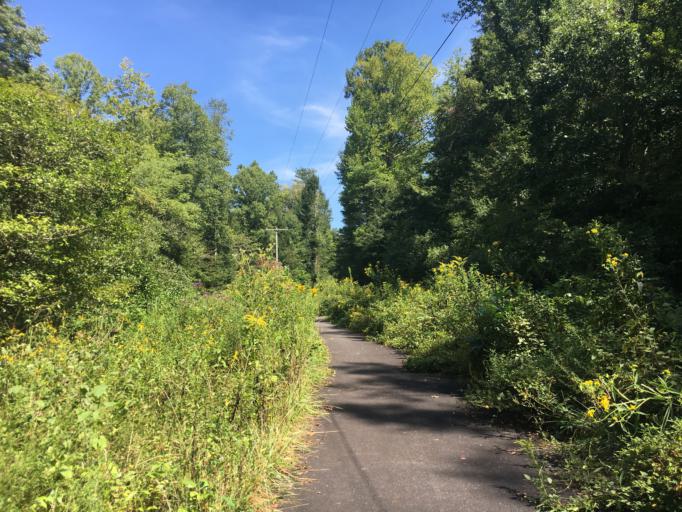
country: US
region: North Carolina
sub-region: Graham County
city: Robbinsville
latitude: 35.2798
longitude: -83.6756
